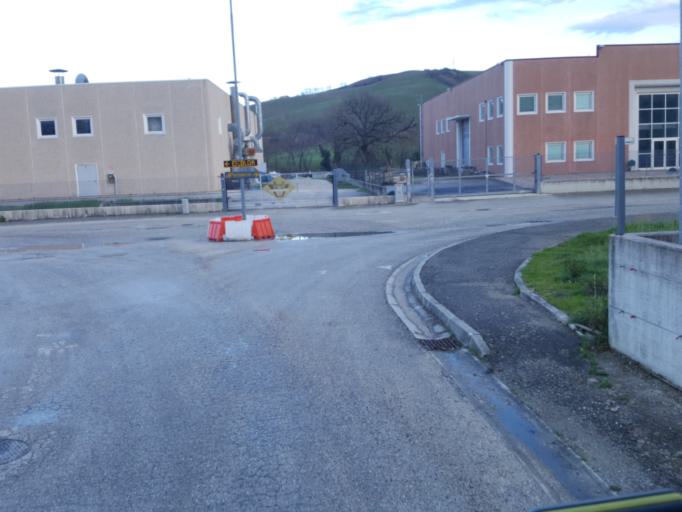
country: IT
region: The Marches
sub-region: Provincia di Macerata
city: San Severino Marche
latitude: 43.2482
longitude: 13.2309
